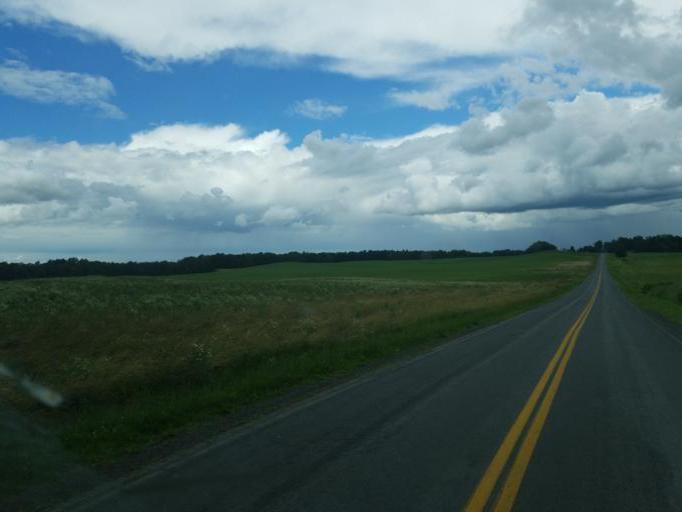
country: US
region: New York
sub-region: Wayne County
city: Lyons
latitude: 42.9790
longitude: -76.9351
